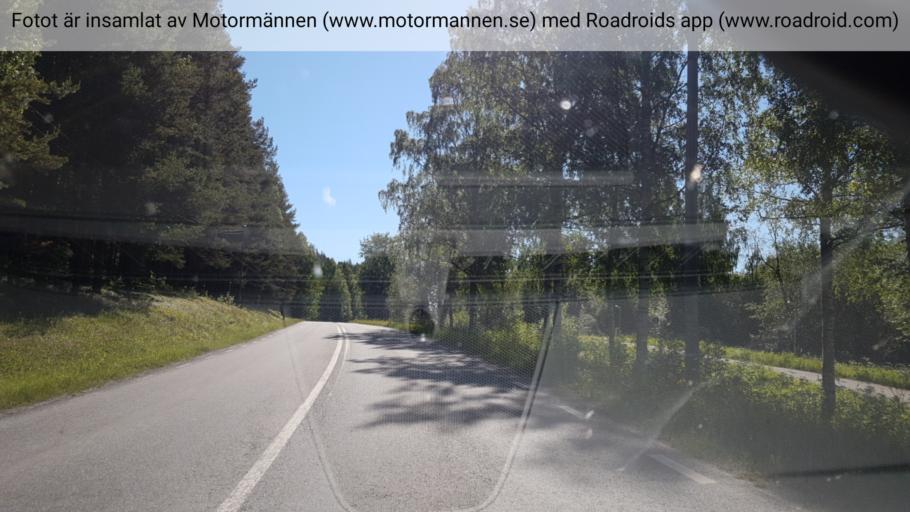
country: SE
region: Norrbotten
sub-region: Bodens Kommun
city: Boden
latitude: 65.8326
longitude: 21.6183
